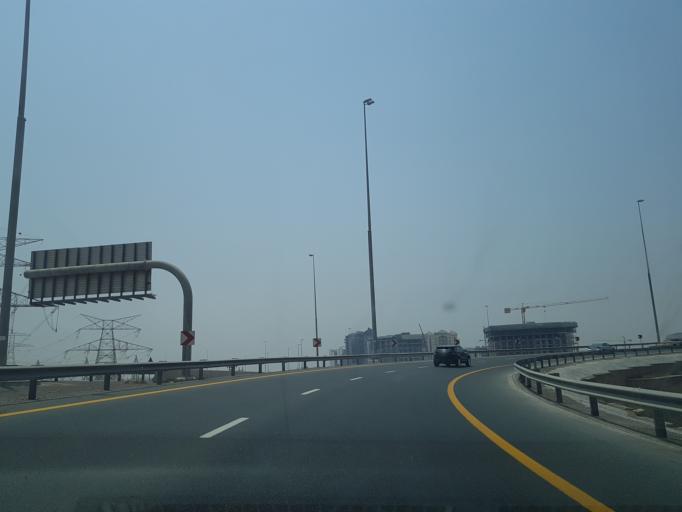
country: AE
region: Dubai
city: Dubai
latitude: 25.0847
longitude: 55.3920
